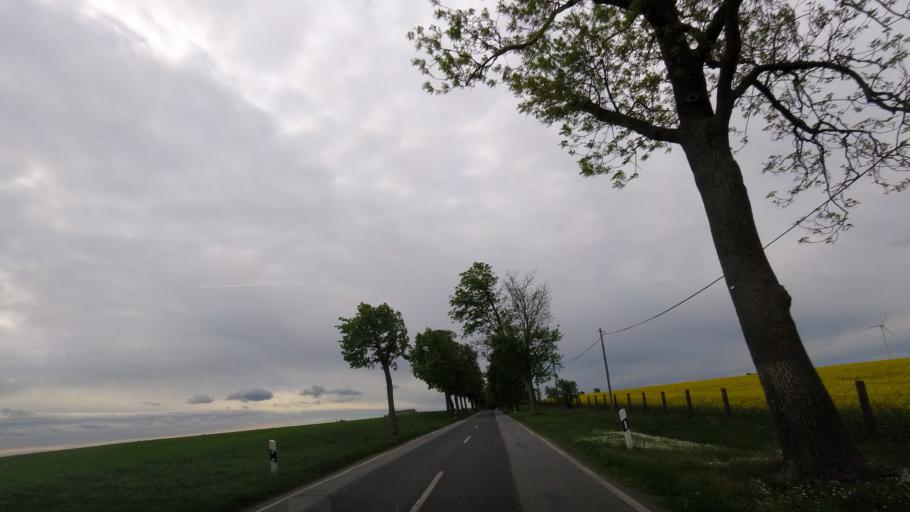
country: DE
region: Brandenburg
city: Dahme
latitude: 51.8844
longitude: 13.4191
